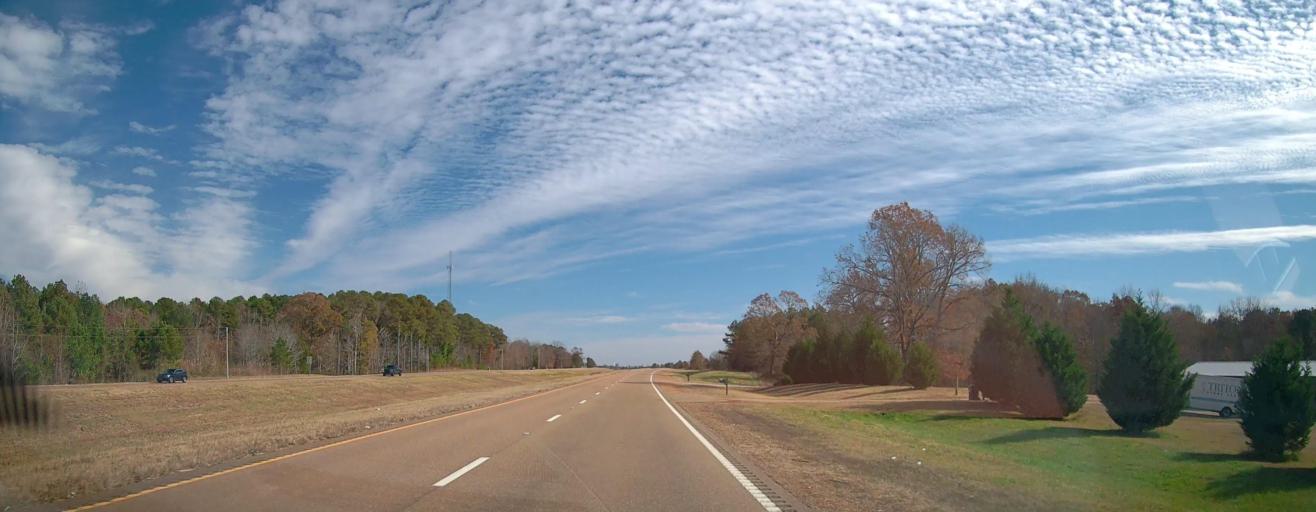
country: US
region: Mississippi
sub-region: Benton County
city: Ashland
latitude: 34.9541
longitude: -89.0219
